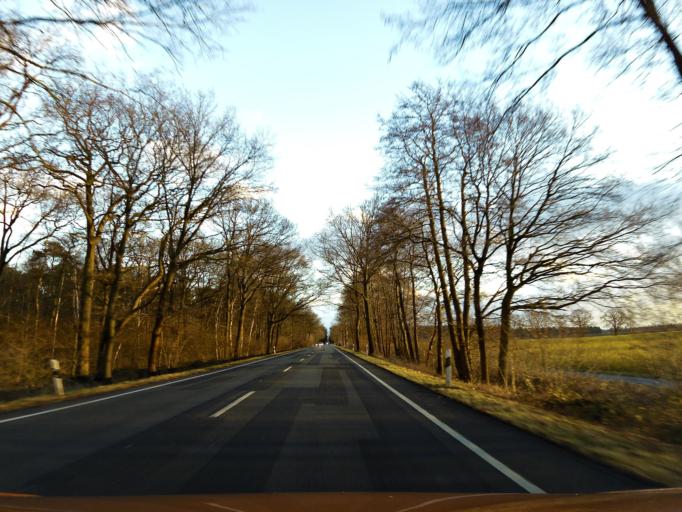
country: DE
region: Lower Saxony
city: Broeckel
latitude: 52.4909
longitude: 10.2442
